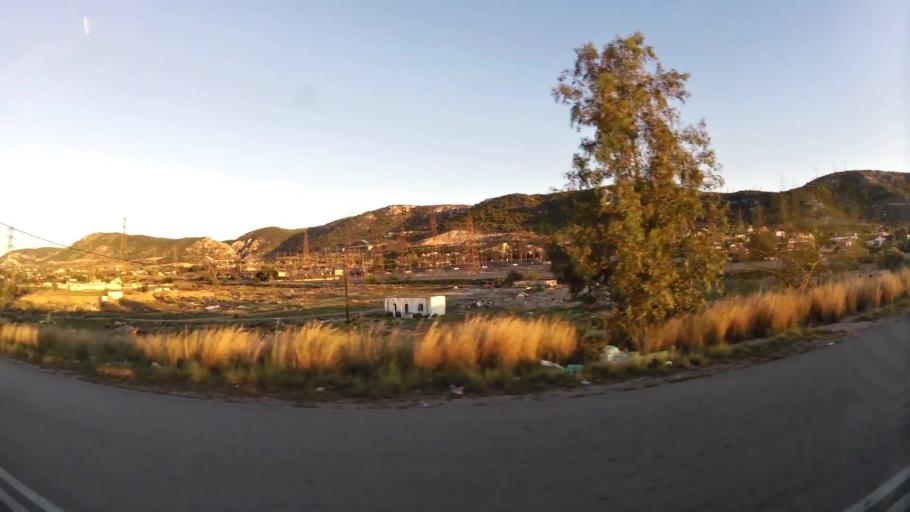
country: GR
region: Attica
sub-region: Nomarchia Athinas
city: Skaramangas
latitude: 38.0343
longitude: 23.6176
